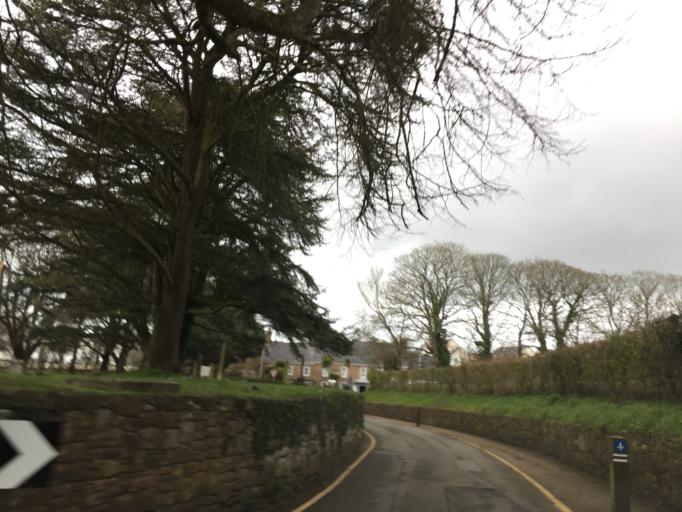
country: JE
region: St Helier
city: Saint Helier
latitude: 49.2345
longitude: -2.1733
